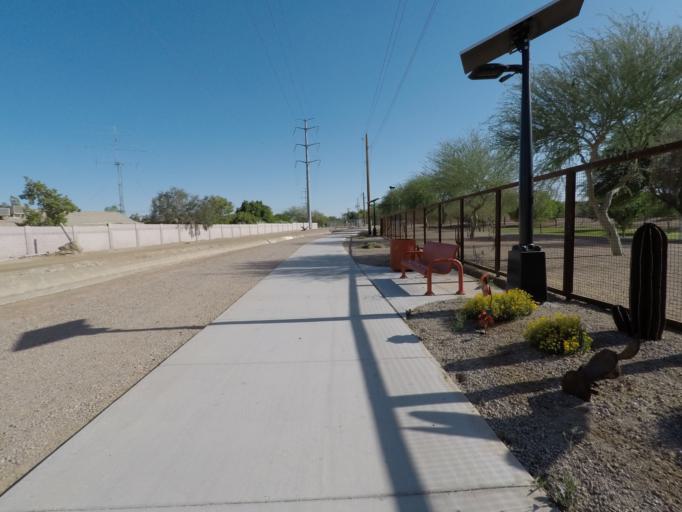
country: US
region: Arizona
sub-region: Maricopa County
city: Guadalupe
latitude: 33.3575
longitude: -111.9565
